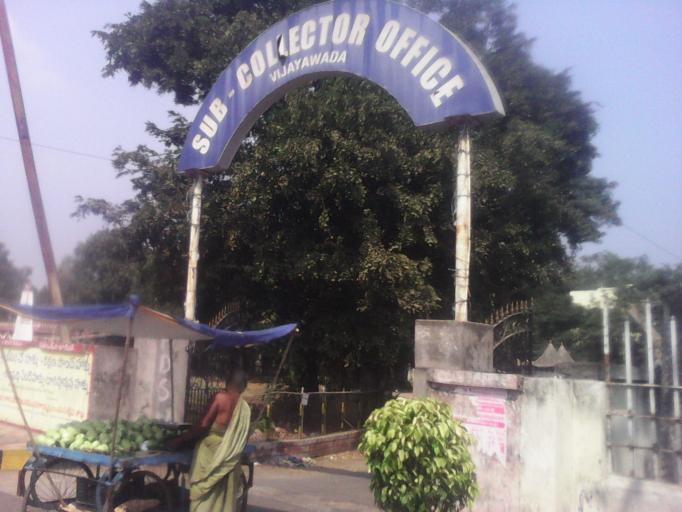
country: IN
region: Andhra Pradesh
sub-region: Krishna
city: Vijayawada
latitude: 16.5068
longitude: 80.6291
